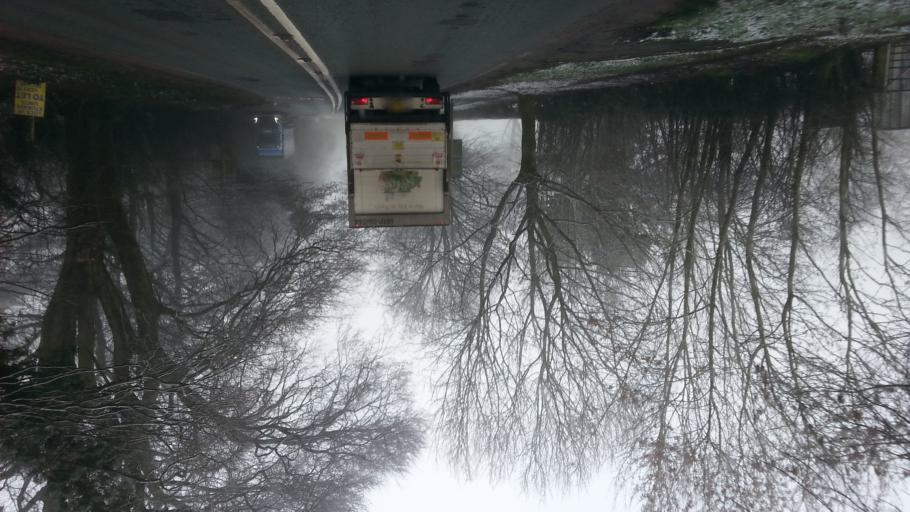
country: GB
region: England
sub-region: Cheshire East
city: Eaton
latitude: 53.1831
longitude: -2.2106
